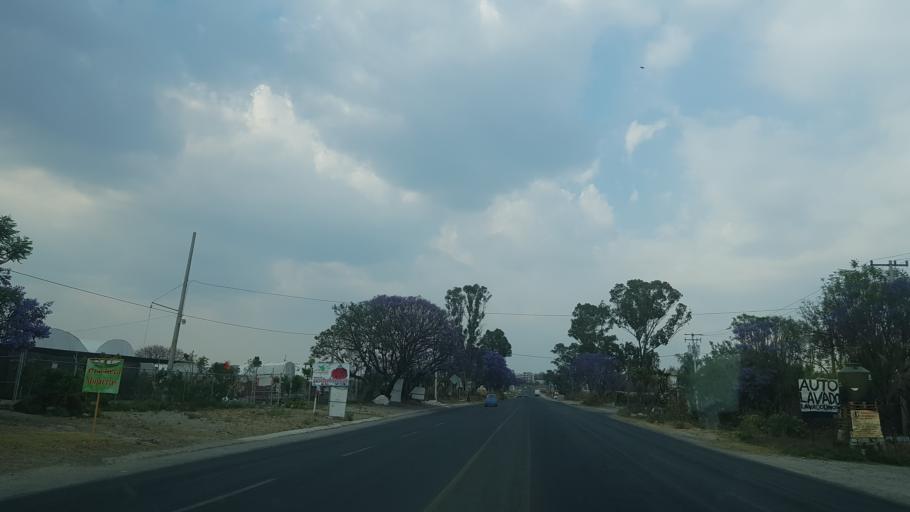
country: MX
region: Puebla
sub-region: Santa Isabel Cholula
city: Santa Ana Acozautla
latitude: 18.9586
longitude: -98.3866
